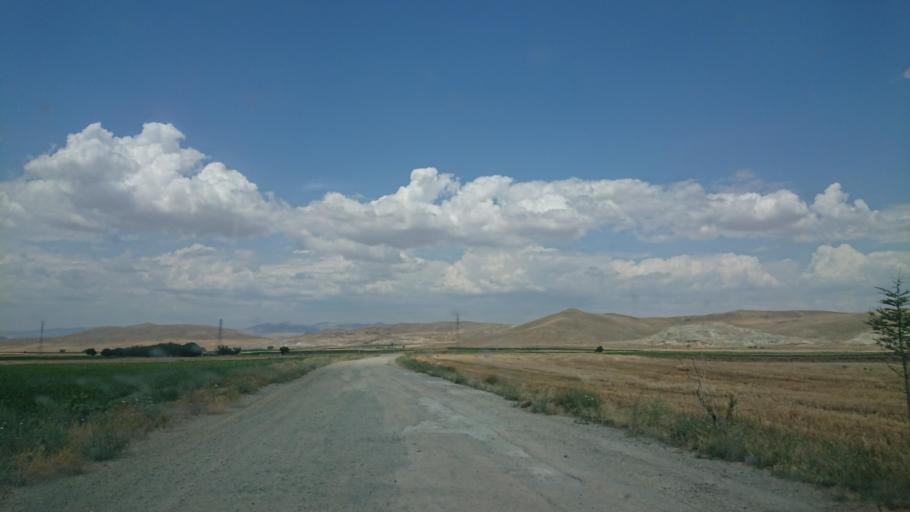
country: TR
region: Aksaray
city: Sariyahsi
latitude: 38.9784
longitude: 33.9023
